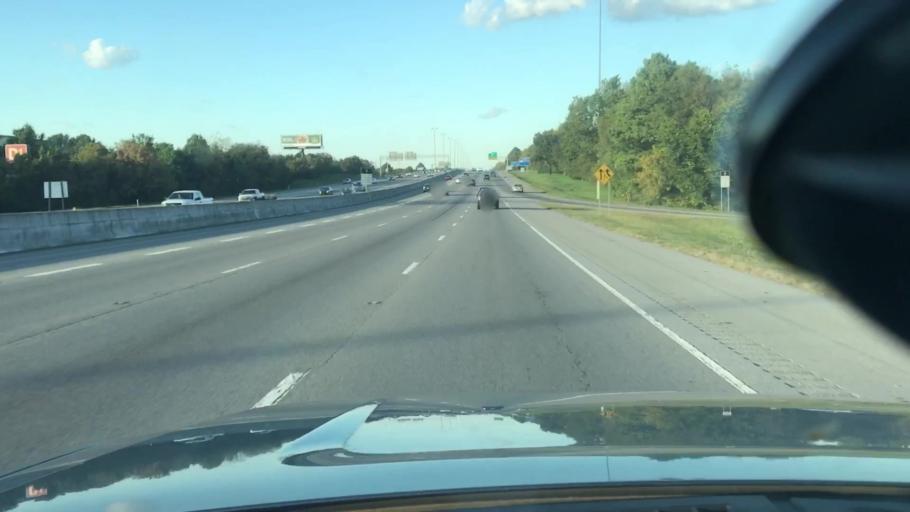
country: US
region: Tennessee
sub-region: Williamson County
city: Franklin
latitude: 35.9505
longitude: -86.8130
